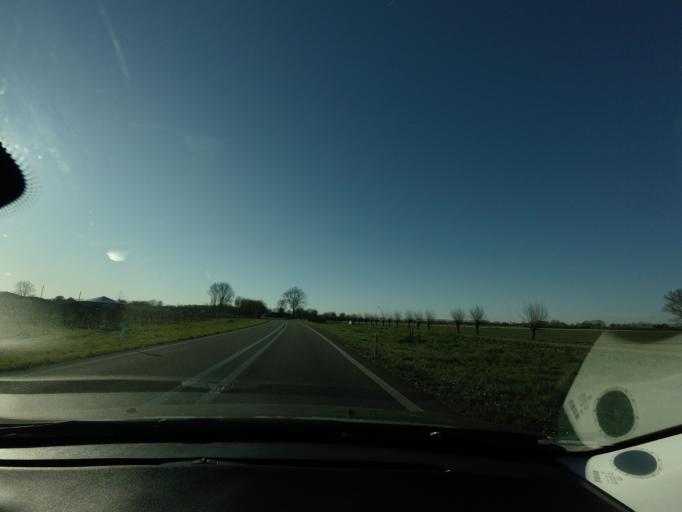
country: NL
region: Gelderland
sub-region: Gemeente Culemborg
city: Culemborg
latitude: 51.9497
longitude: 5.2661
